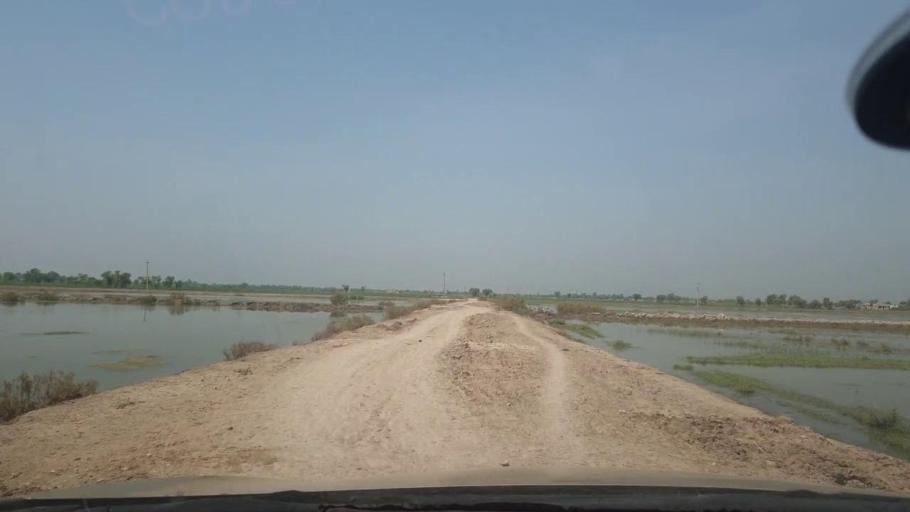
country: PK
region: Sindh
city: Shahdadkot
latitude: 27.7539
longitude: 67.9304
